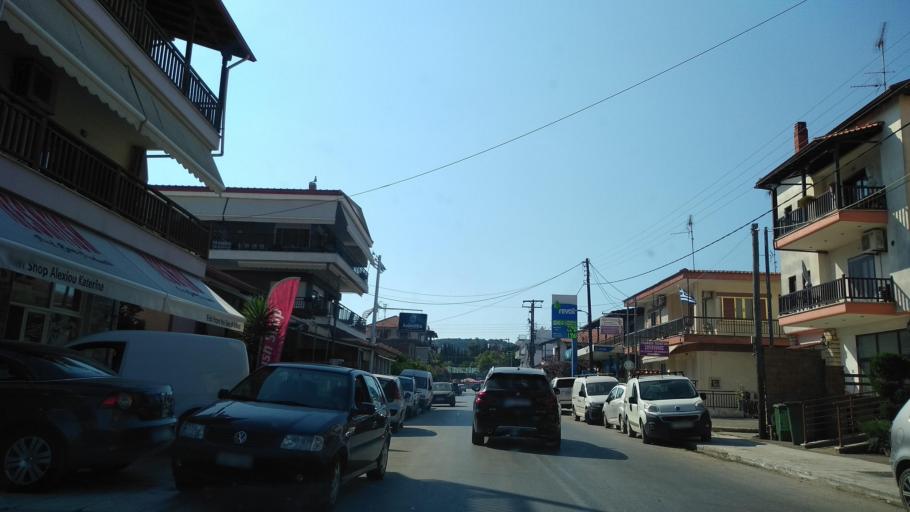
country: GR
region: Central Macedonia
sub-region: Nomos Chalkidikis
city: Ierissos
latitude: 40.3988
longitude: 23.8732
